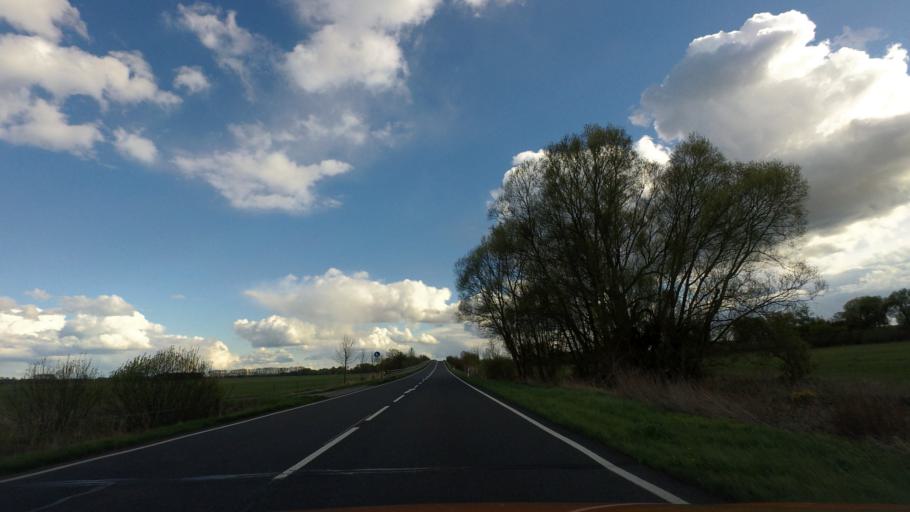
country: DE
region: Brandenburg
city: Friesack
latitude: 52.7859
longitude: 12.5547
